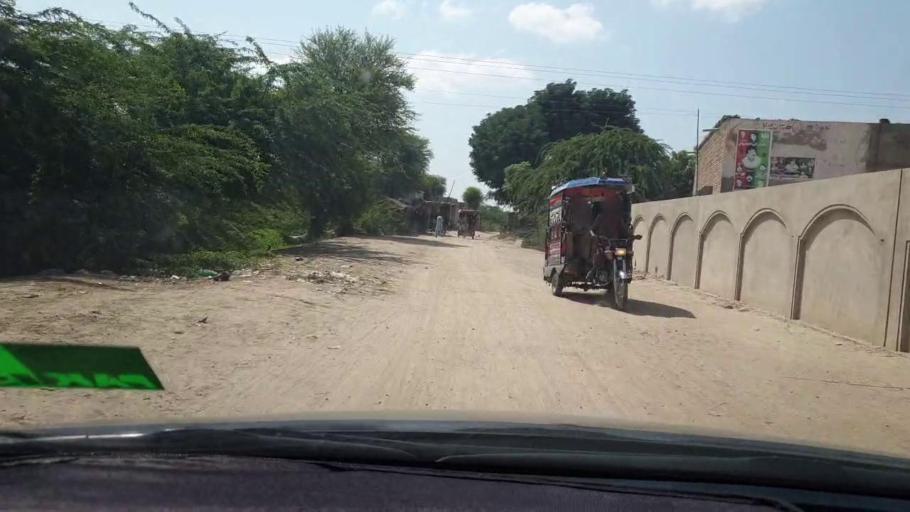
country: PK
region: Sindh
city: Naukot
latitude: 24.9149
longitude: 69.2601
